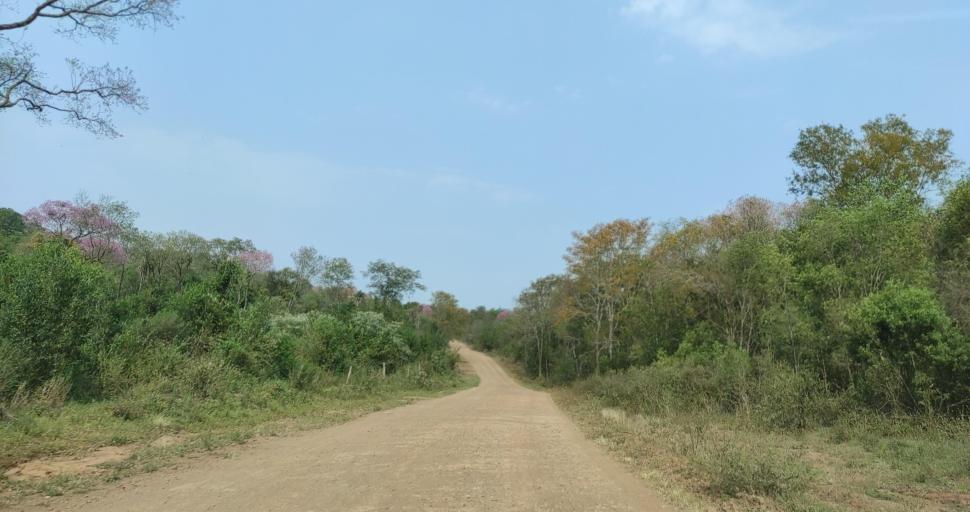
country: AR
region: Misiones
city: Cerro Cora
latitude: -27.5308
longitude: -55.5935
